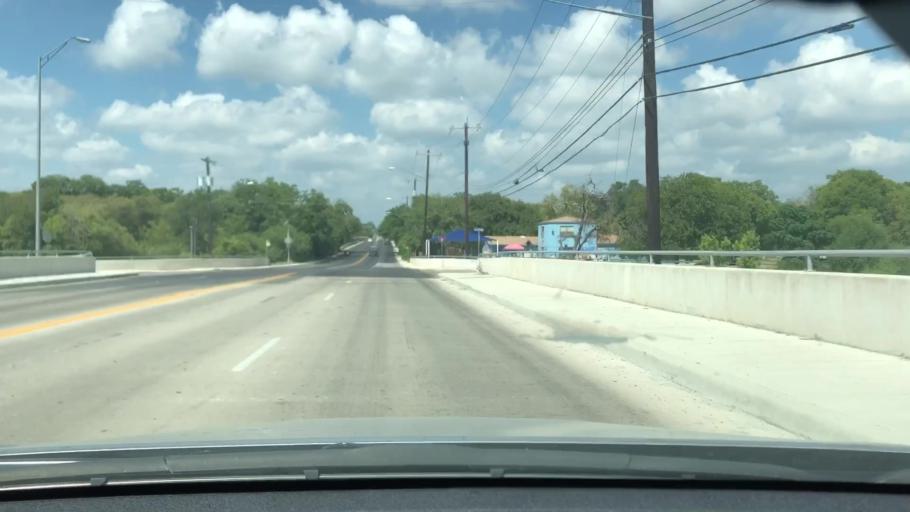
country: US
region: Texas
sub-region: Bexar County
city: Terrell Hills
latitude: 29.4849
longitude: -98.4175
